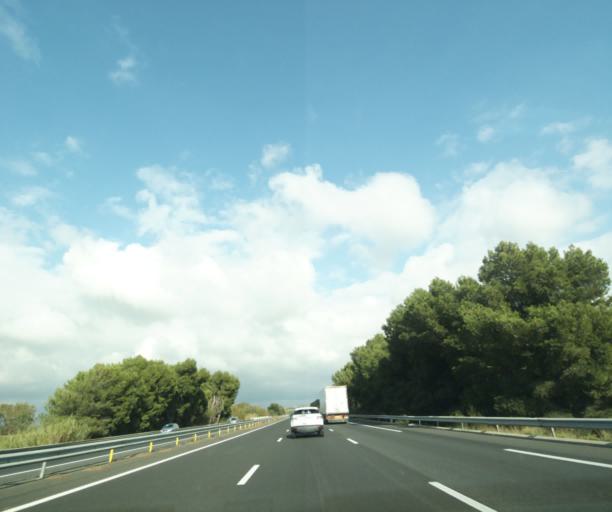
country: FR
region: Languedoc-Roussillon
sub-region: Departement de l'Aude
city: Fleury
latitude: 43.2441
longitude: 3.1497
